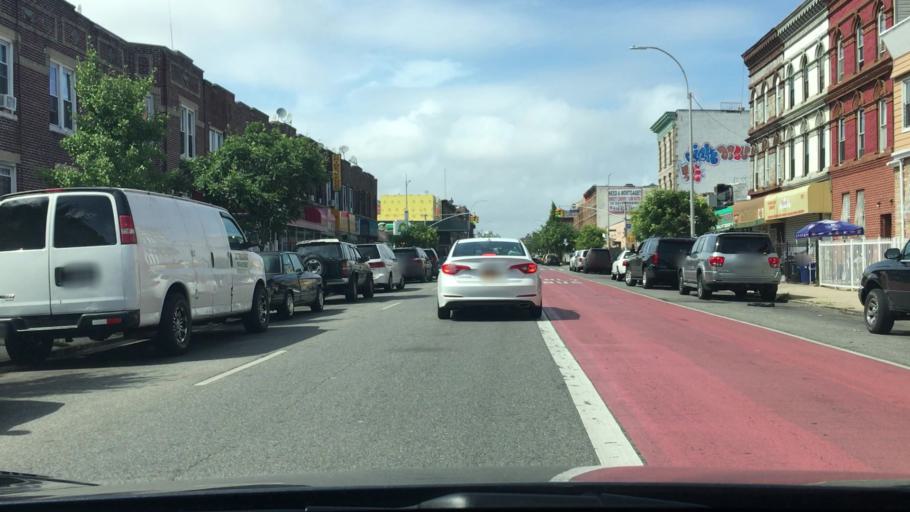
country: US
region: New York
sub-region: Kings County
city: Brooklyn
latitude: 40.6423
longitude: -73.9516
